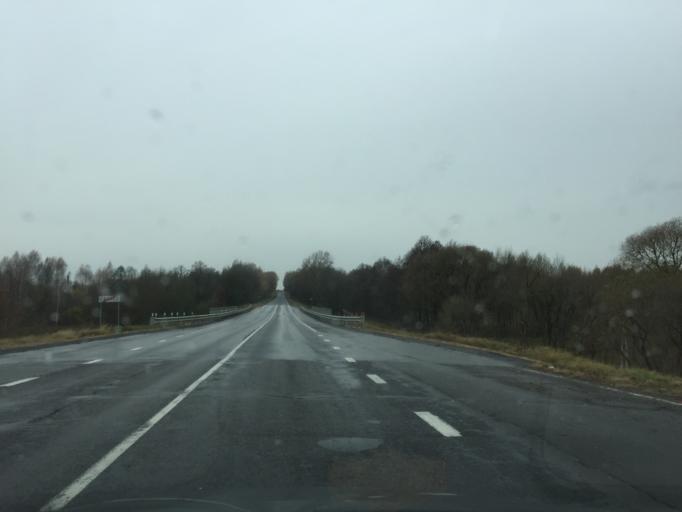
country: BY
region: Gomel
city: Karma
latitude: 53.3398
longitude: 30.8005
